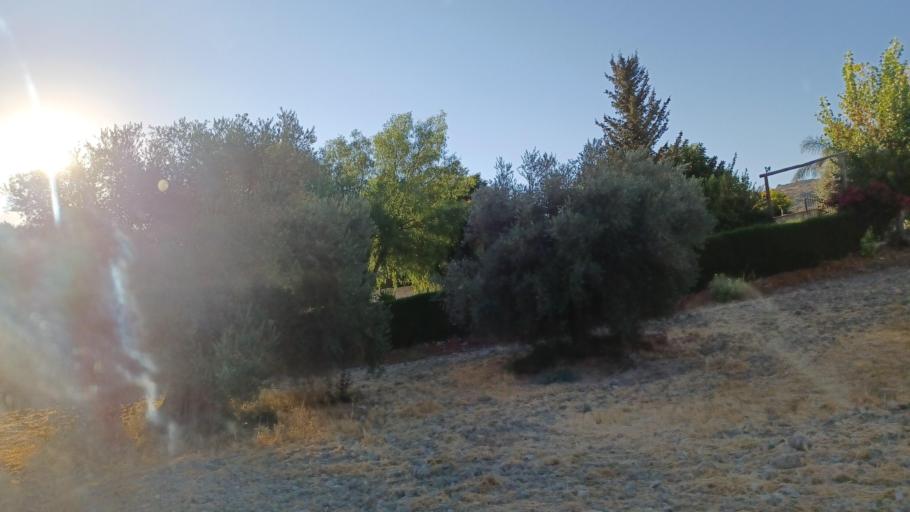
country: CY
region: Pafos
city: Polis
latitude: 34.9813
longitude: 32.4615
